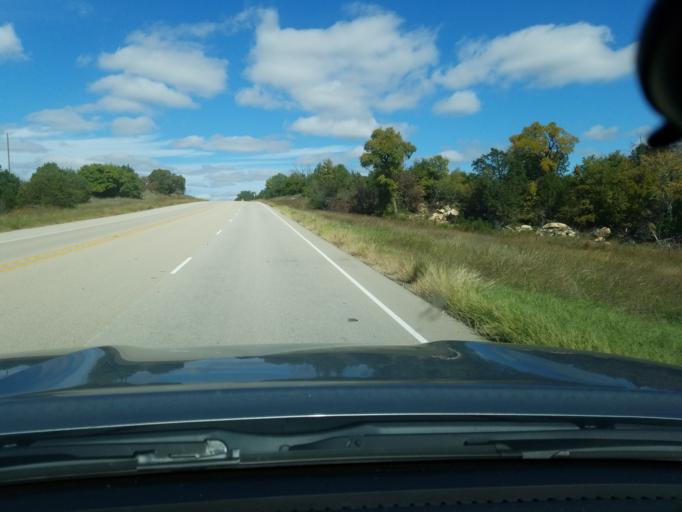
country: US
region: Texas
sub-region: Hamilton County
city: Hamilton
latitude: 31.5861
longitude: -98.1567
